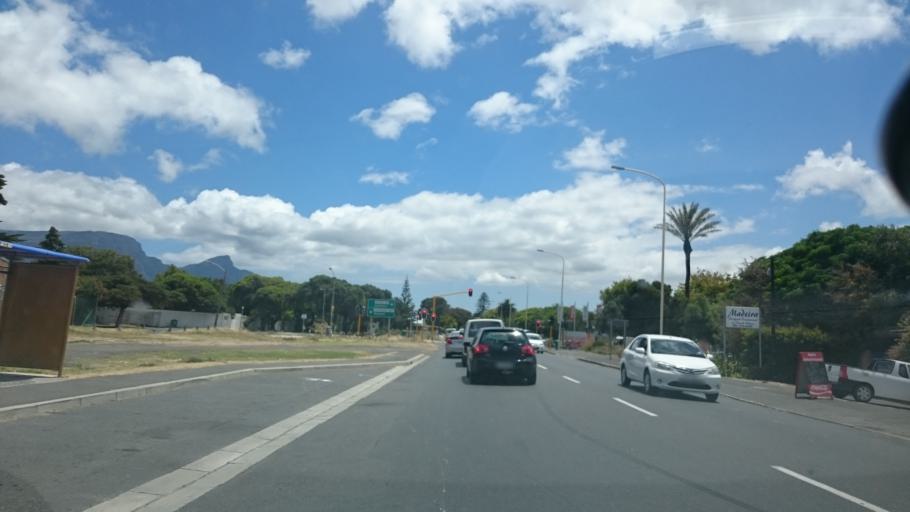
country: ZA
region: Western Cape
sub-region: City of Cape Town
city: Bergvliet
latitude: -34.0515
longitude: 18.4617
